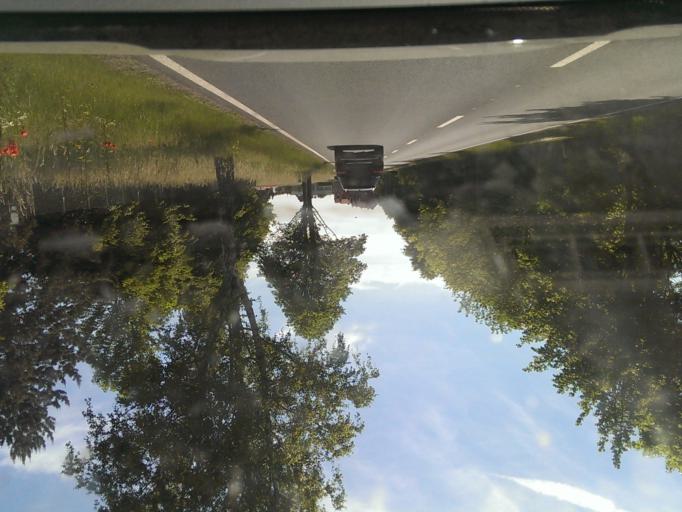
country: DE
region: Lower Saxony
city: Alfeld
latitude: 52.0017
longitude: 9.7979
